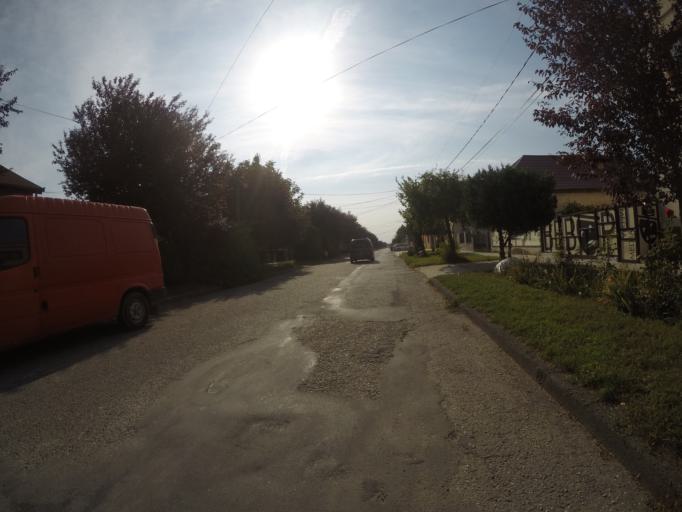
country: SK
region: Trnavsky
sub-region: Okres Dunajska Streda
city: Velky Meder
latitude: 47.8558
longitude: 17.7619
